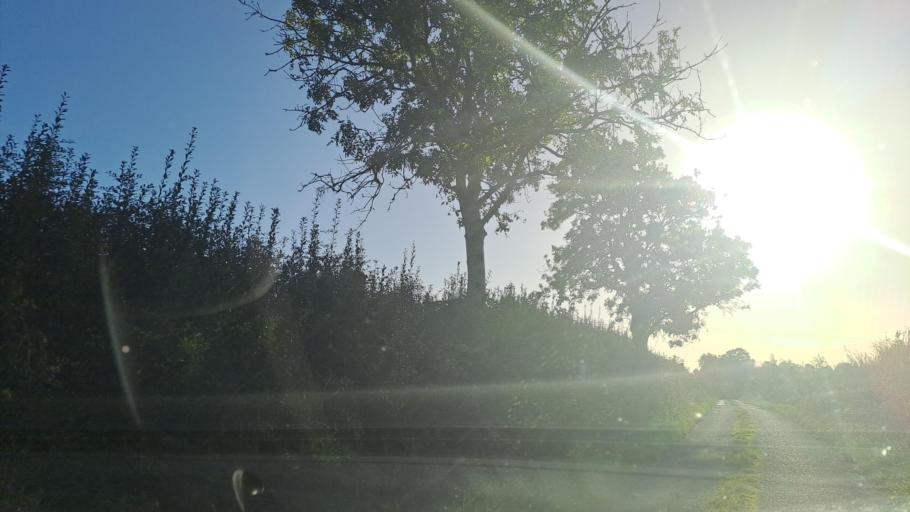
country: IE
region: Ulster
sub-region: An Cabhan
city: Kingscourt
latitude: 53.9817
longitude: -6.8447
